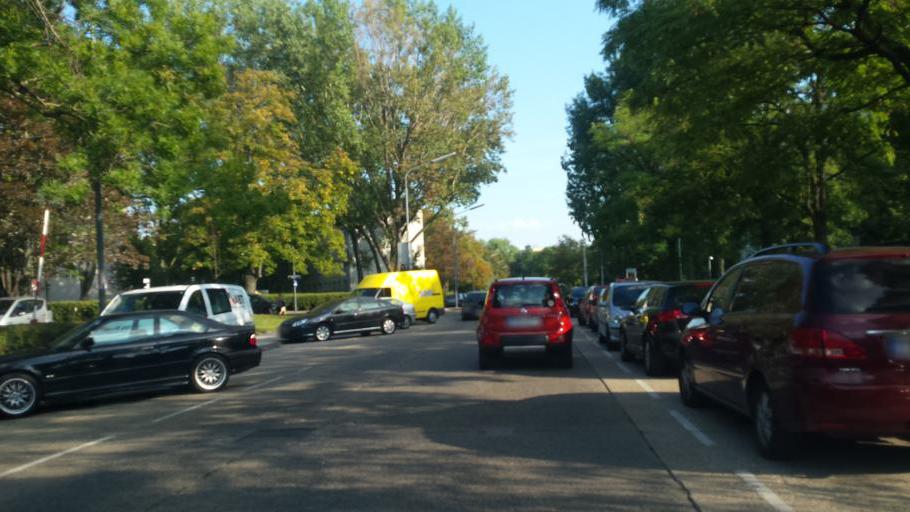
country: AT
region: Lower Austria
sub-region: Politischer Bezirk Wien-Umgebung
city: Leopoldsdorf
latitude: 48.1479
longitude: 16.3868
